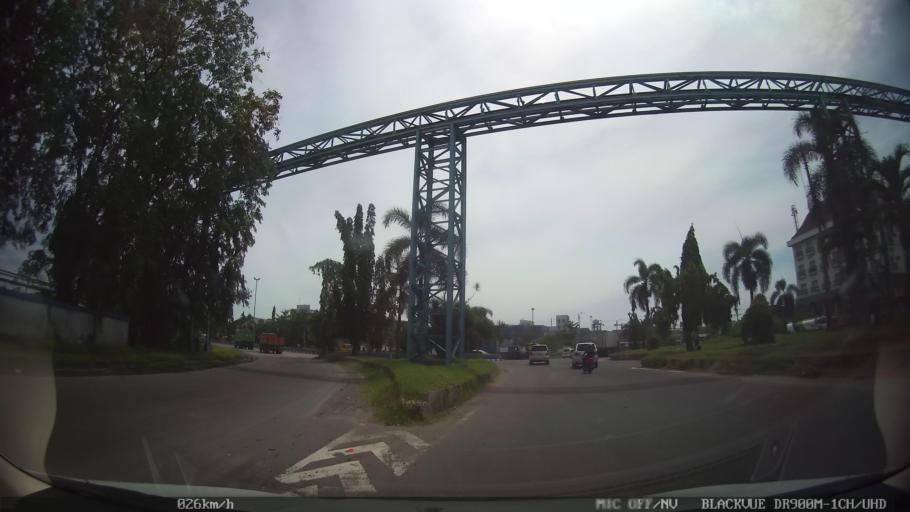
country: ID
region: North Sumatra
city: Belawan
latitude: 3.7814
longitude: 98.6927
